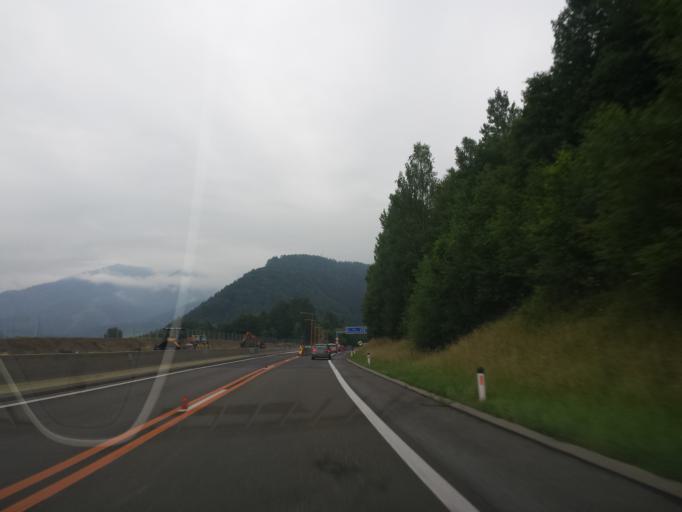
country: AT
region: Styria
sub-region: Politischer Bezirk Bruck-Muerzzuschlag
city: Muerzzuschlag
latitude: 47.5837
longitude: 15.6592
